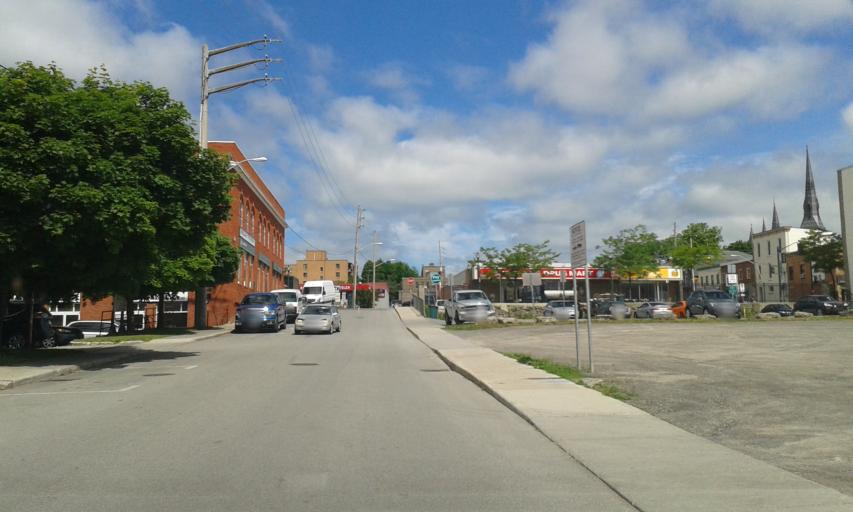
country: CA
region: Ontario
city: Brockville
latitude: 44.5877
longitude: -75.6856
